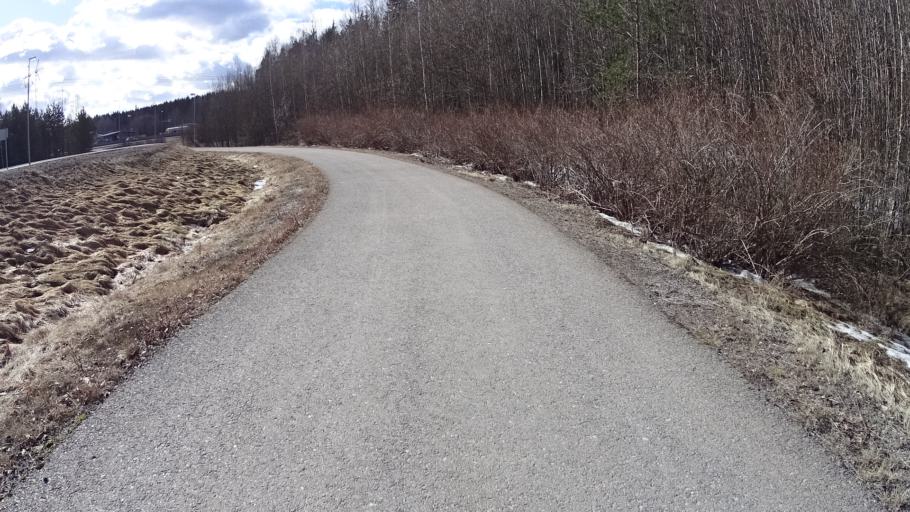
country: FI
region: Uusimaa
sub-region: Helsinki
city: Kauniainen
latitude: 60.2631
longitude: 24.7303
